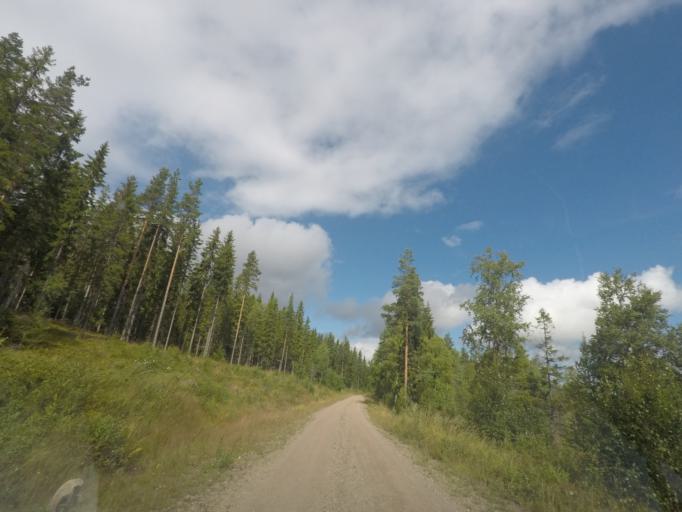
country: SE
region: Vaermland
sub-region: Filipstads Kommun
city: Lesjofors
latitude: 60.0478
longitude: 14.4429
